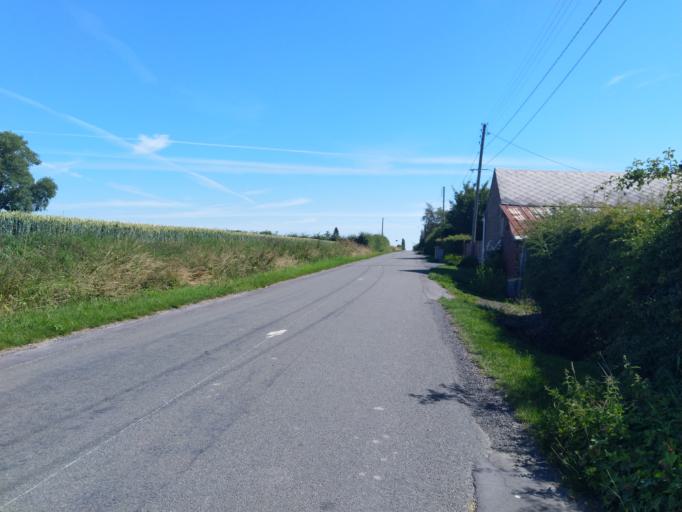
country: FR
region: Nord-Pas-de-Calais
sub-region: Departement du Nord
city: La Longueville
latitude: 50.3338
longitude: 3.8385
